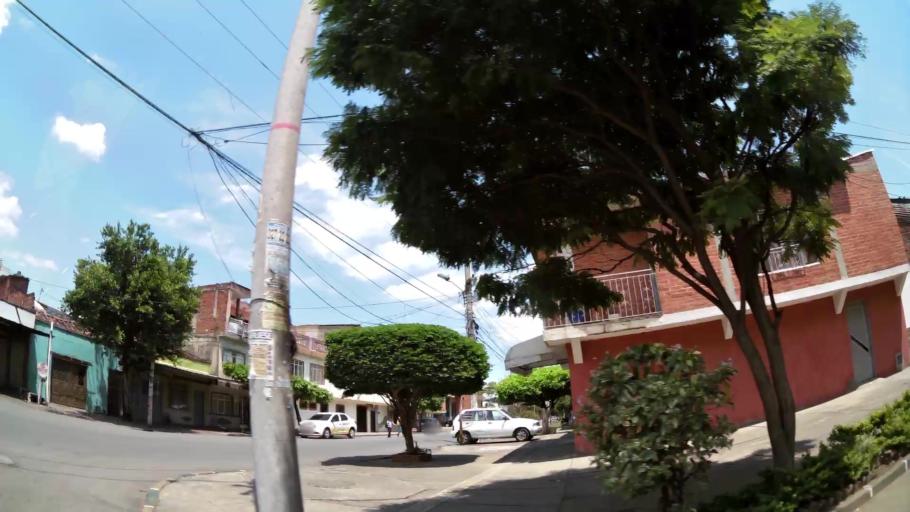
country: CO
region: Valle del Cauca
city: Cali
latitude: 3.4497
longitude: -76.5104
